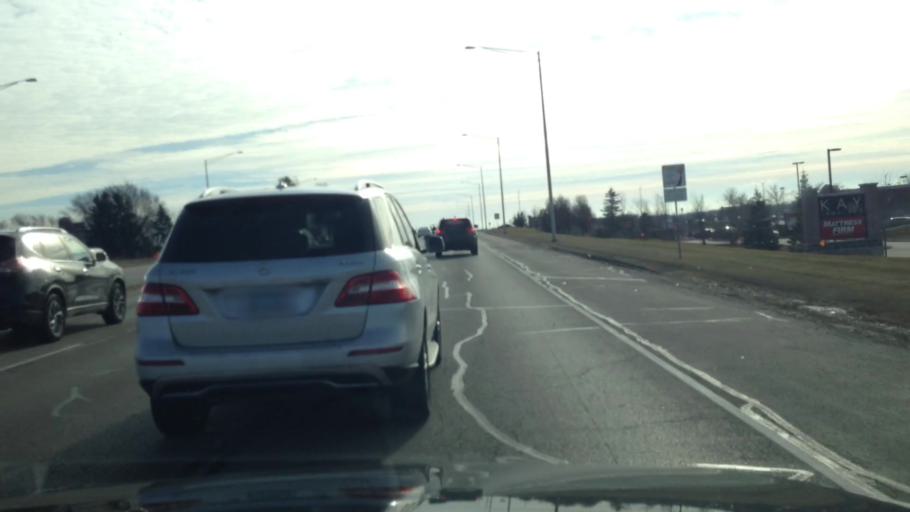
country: US
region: Illinois
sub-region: McHenry County
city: Lake in the Hills
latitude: 42.1603
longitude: -88.3358
